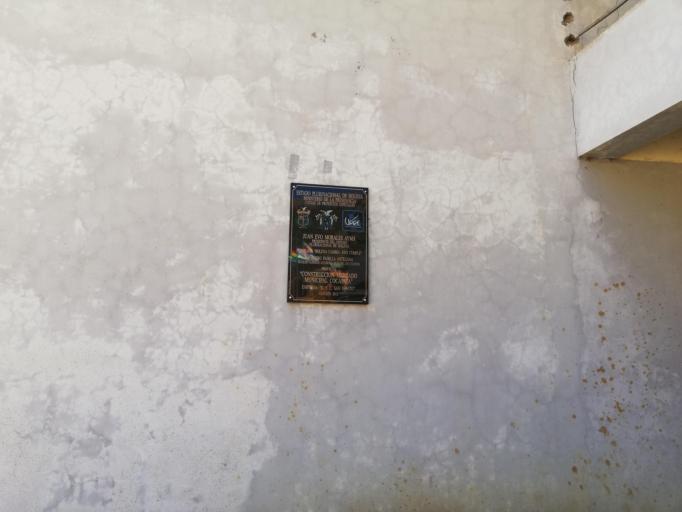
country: BO
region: Cochabamba
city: Colchani
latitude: -16.7999
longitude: -66.6692
